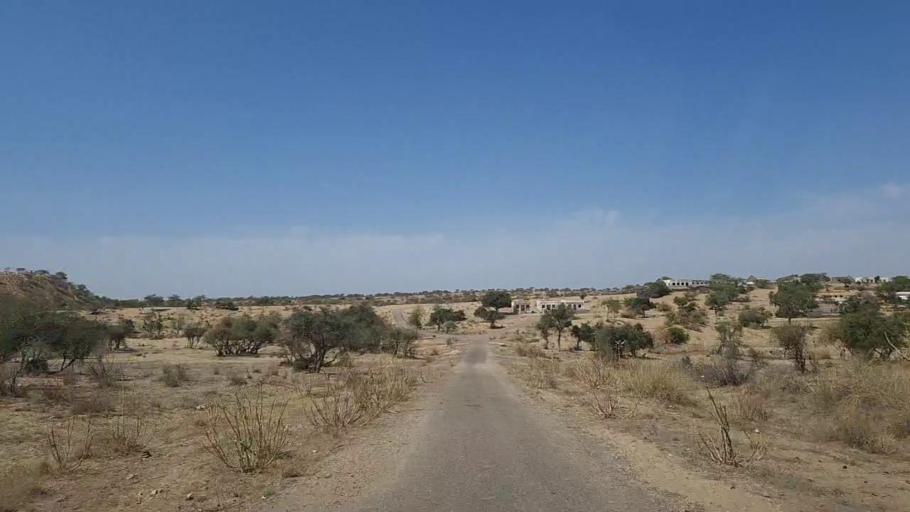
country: PK
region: Sindh
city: Mithi
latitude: 24.8670
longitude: 69.6612
